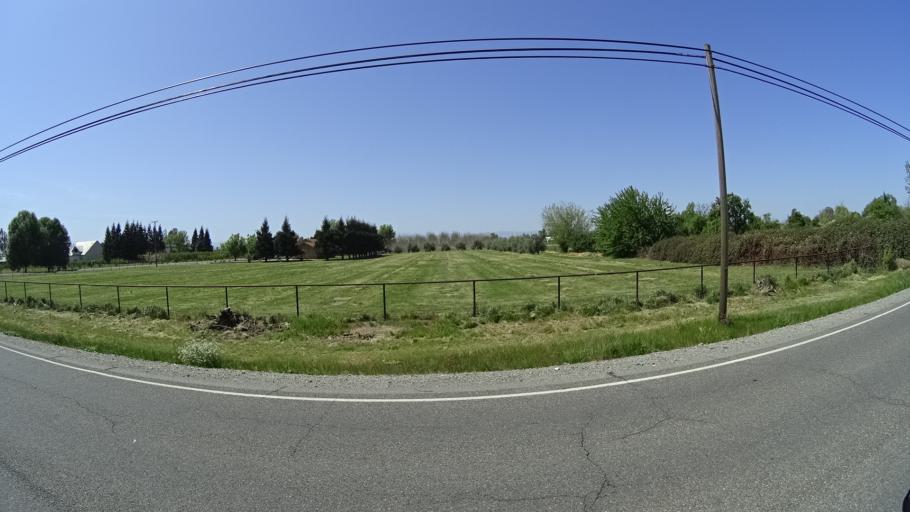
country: US
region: California
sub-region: Glenn County
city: Orland
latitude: 39.7200
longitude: -122.1970
